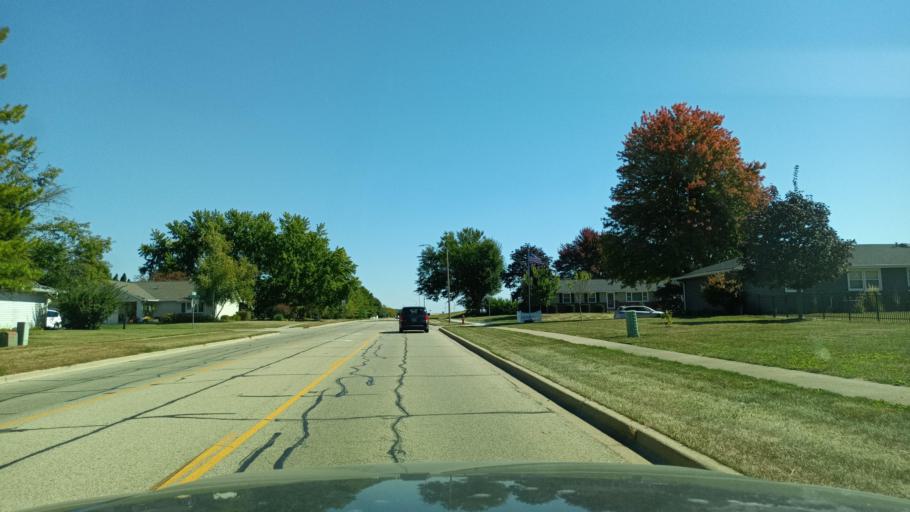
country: US
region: Illinois
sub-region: Tazewell County
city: Morton
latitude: 40.6132
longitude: -89.4423
